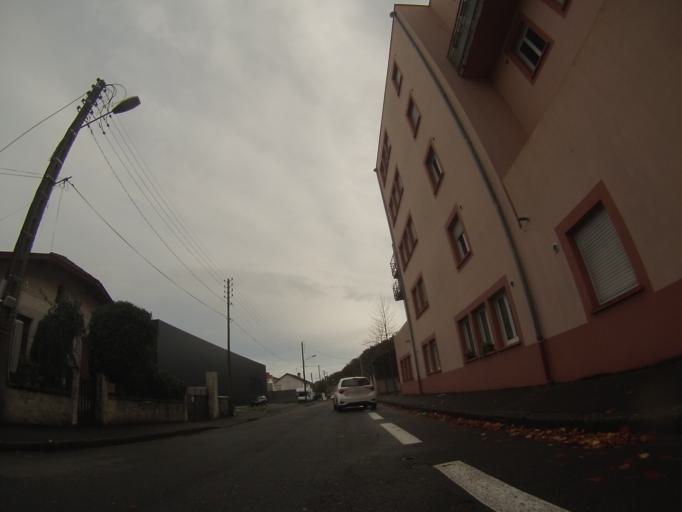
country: FR
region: Aquitaine
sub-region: Departement des Pyrenees-Atlantiques
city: Jurancon
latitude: 43.2834
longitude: -0.3862
